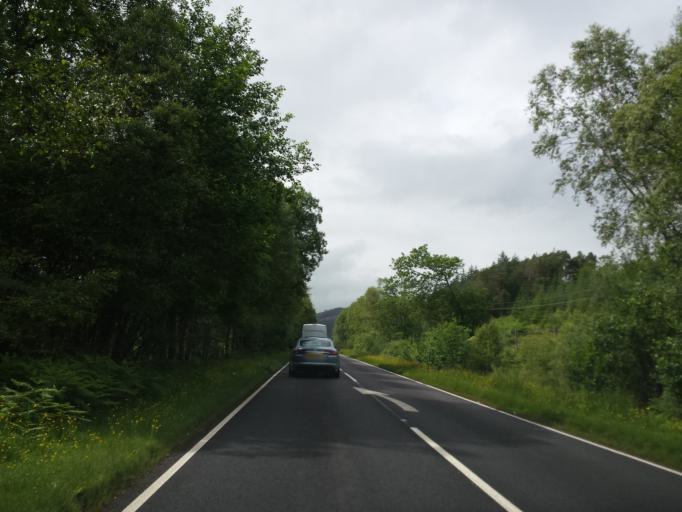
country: GB
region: Scotland
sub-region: Highland
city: Fort William
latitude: 56.8619
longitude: -5.3775
